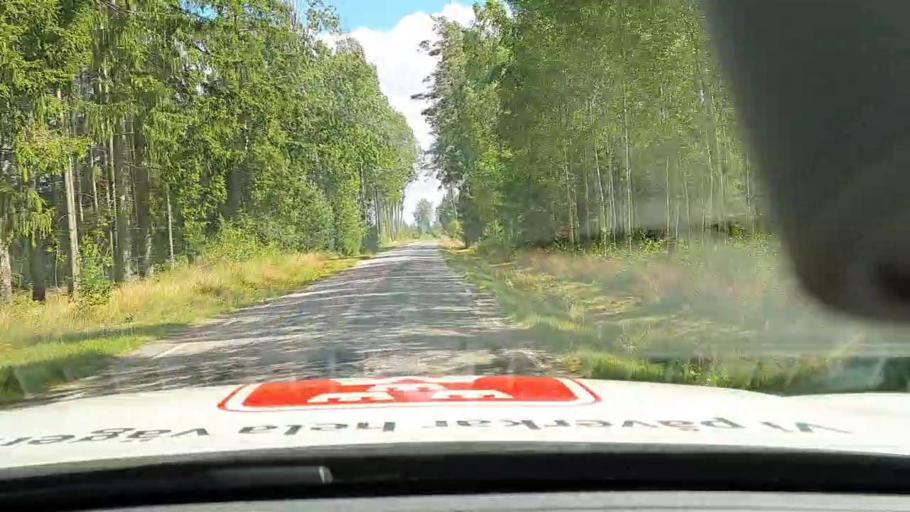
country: SE
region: Vaestra Goetaland
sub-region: Toreboda Kommun
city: Toereboda
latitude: 58.5689
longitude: 14.1340
